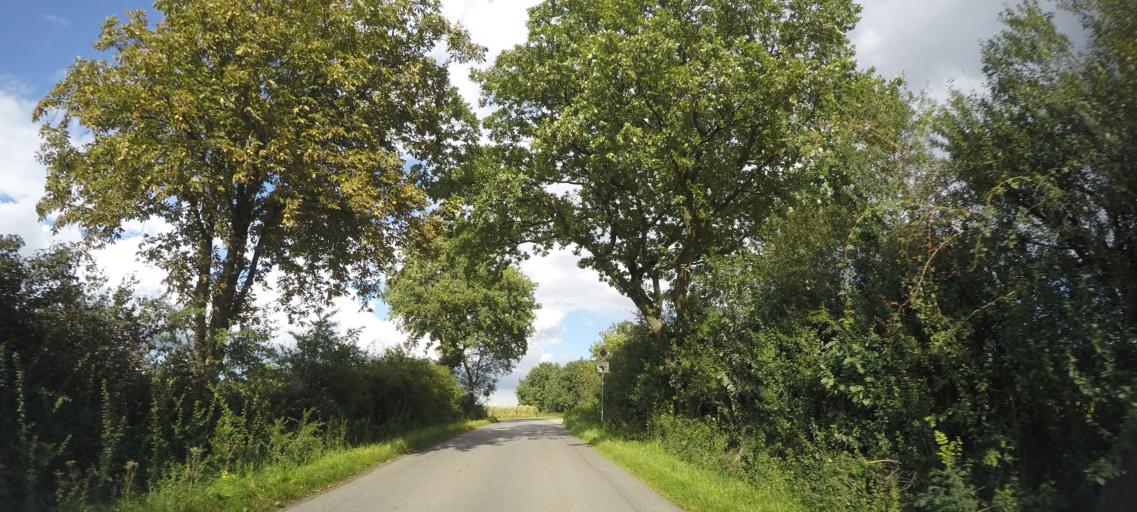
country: DE
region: North Rhine-Westphalia
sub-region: Regierungsbezirk Arnsberg
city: Frondenberg
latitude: 51.4888
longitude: 7.7306
